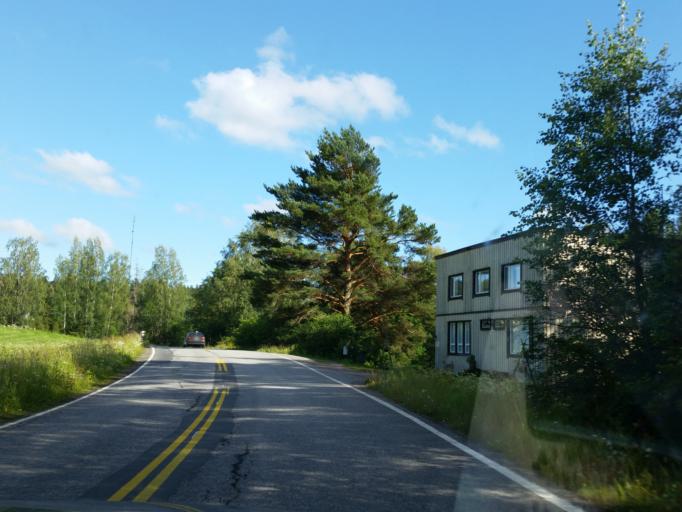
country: FI
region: Uusimaa
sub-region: Helsinki
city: Saukkola
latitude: 60.4822
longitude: 23.9701
